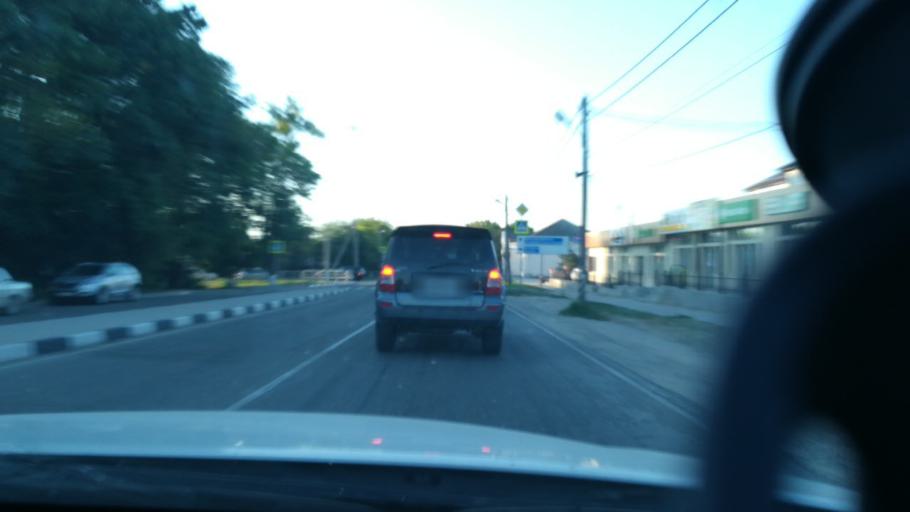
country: RU
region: Krasnodarskiy
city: Gostagayevskaya
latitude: 45.0248
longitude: 37.5032
